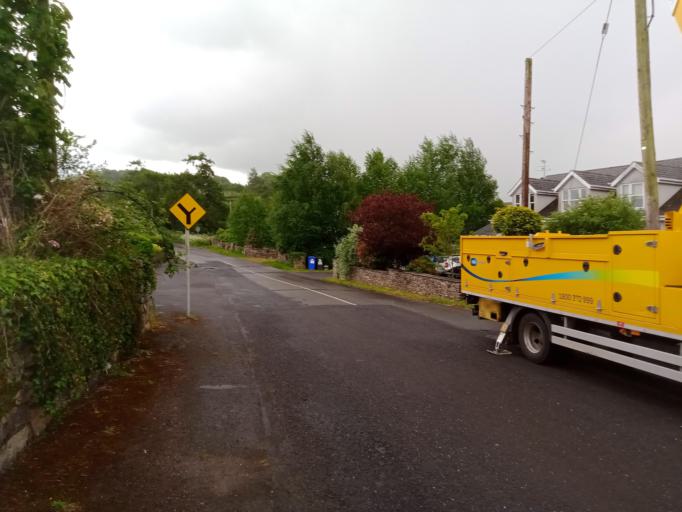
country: IE
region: Leinster
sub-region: Kilkenny
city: Thomastown
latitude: 52.5193
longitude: -7.1352
